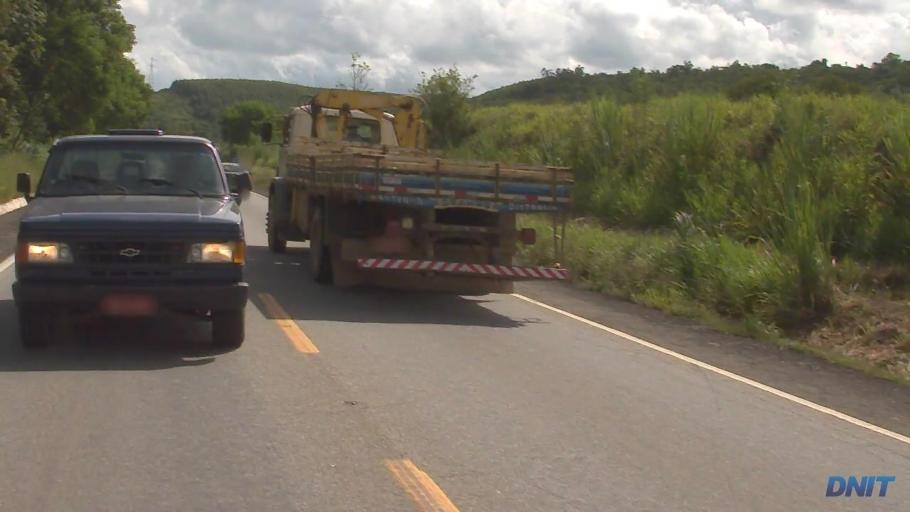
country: BR
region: Minas Gerais
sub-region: Ipaba
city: Ipaba
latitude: -19.3957
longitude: -42.4841
